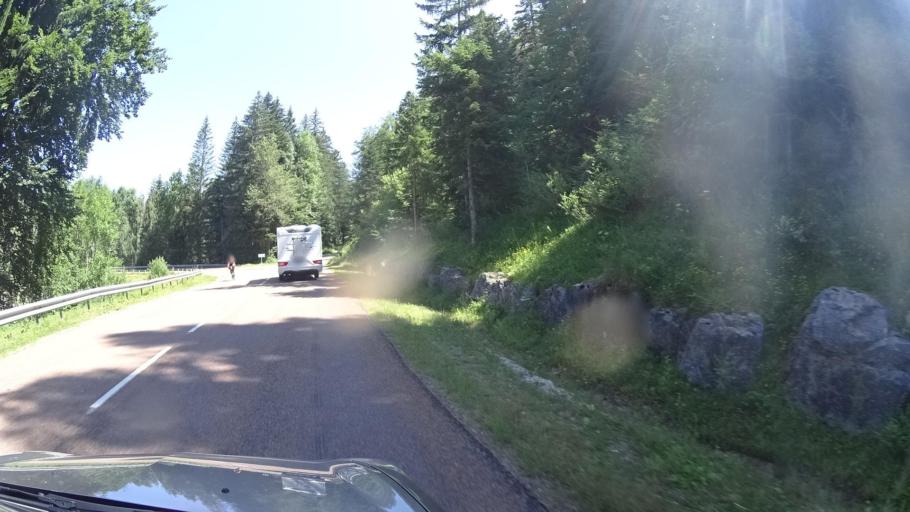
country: FR
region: Franche-Comte
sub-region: Departement du Jura
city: Longchaumois
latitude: 46.5073
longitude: 5.9013
